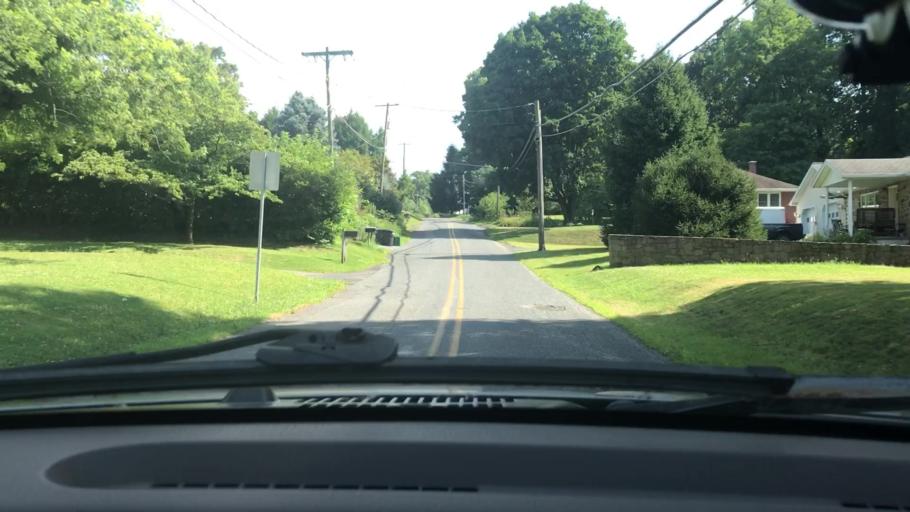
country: US
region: Pennsylvania
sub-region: Lancaster County
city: Elizabethtown
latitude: 40.1726
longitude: -76.6074
